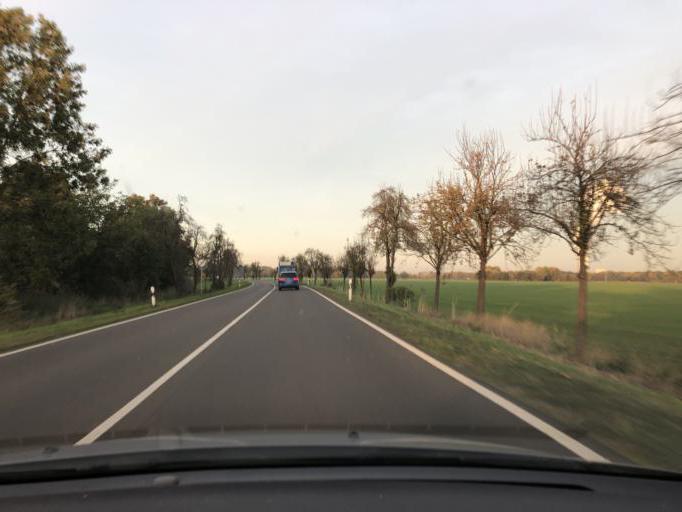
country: DE
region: Saxony
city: Elstertrebnitz
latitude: 51.1471
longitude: 12.2442
